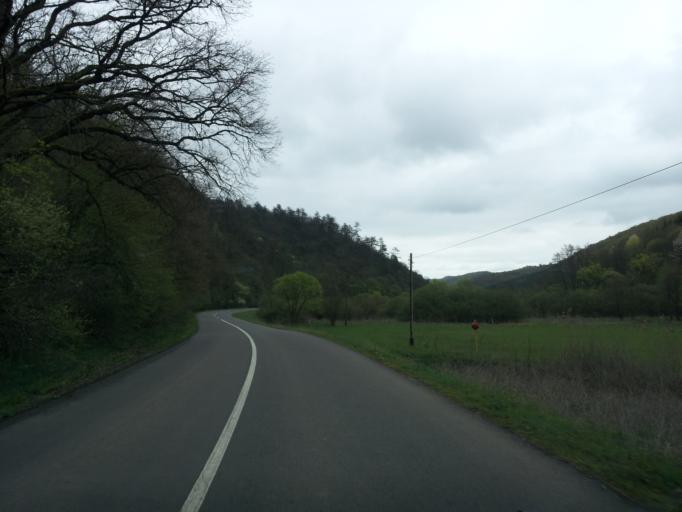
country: HU
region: Borsod-Abauj-Zemplen
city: Rudabanya
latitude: 48.4785
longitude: 20.5801
